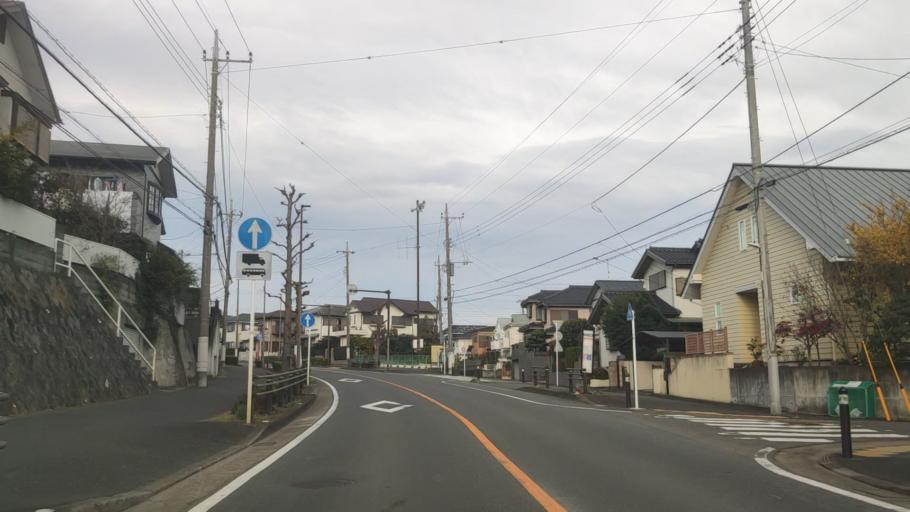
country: JP
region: Kanagawa
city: Atsugi
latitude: 35.4411
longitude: 139.4026
